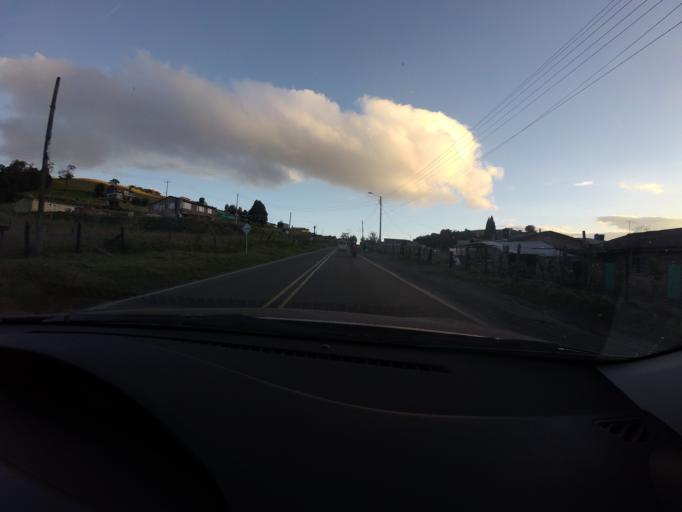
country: CO
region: Cundinamarca
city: Sutatausa
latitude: 5.1838
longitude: -73.8790
